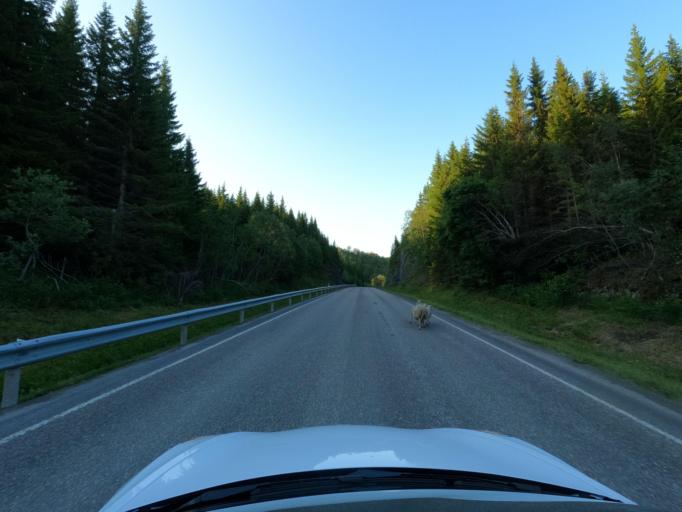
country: NO
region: Troms
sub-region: Harstad
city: Harstad
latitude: 68.7177
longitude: 16.5089
